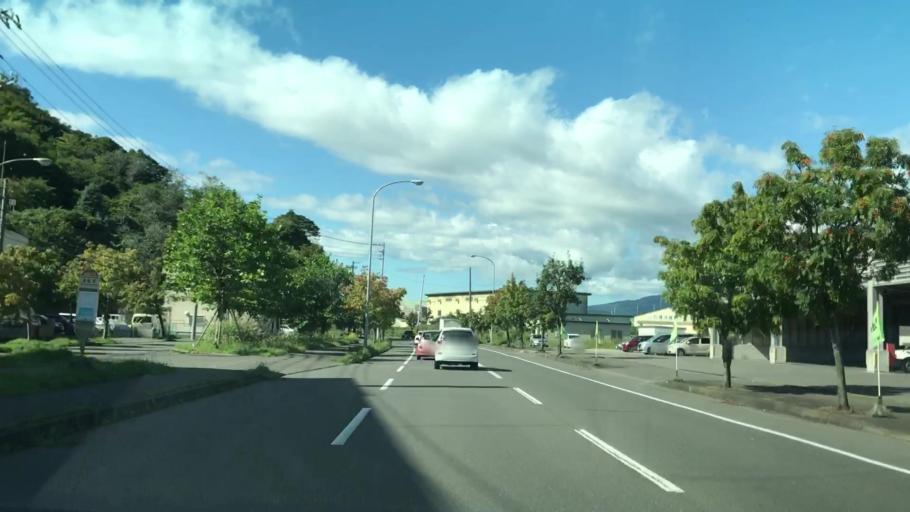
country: JP
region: Hokkaido
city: Muroran
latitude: 42.3280
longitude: 140.9678
